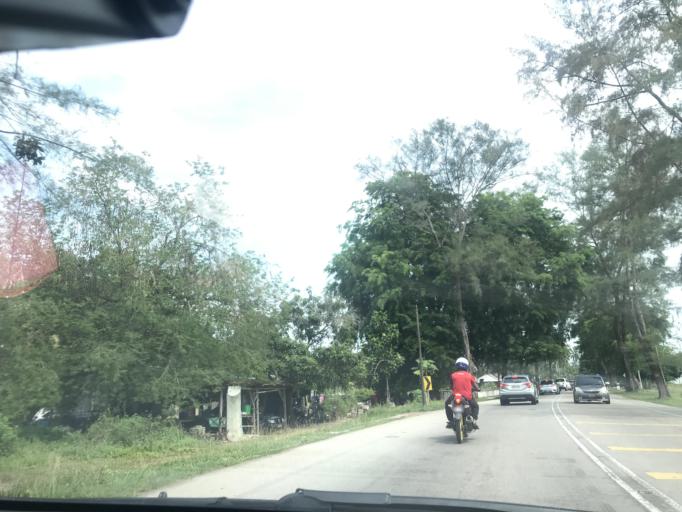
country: MY
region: Kelantan
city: Tumpat
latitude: 6.2106
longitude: 102.1335
